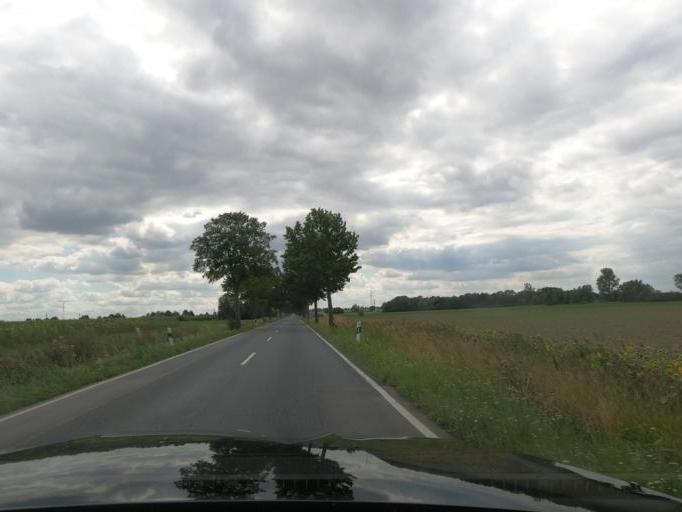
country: DE
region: Lower Saxony
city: Lehrte
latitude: 52.3397
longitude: 10.0281
